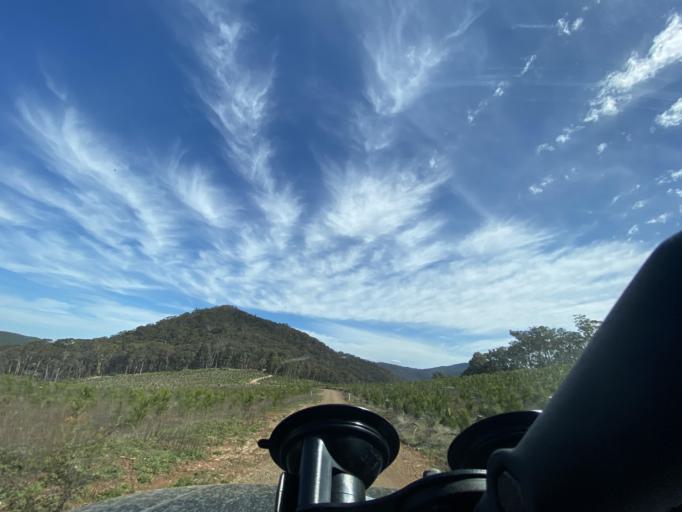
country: AU
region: Victoria
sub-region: Mansfield
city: Mansfield
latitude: -36.8296
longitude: 146.1021
